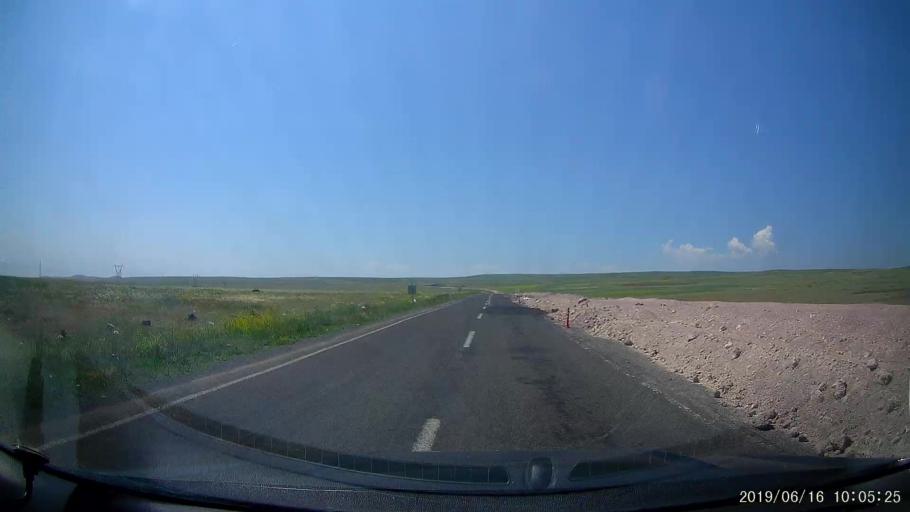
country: TR
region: Kars
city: Digor
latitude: 40.2708
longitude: 43.5383
